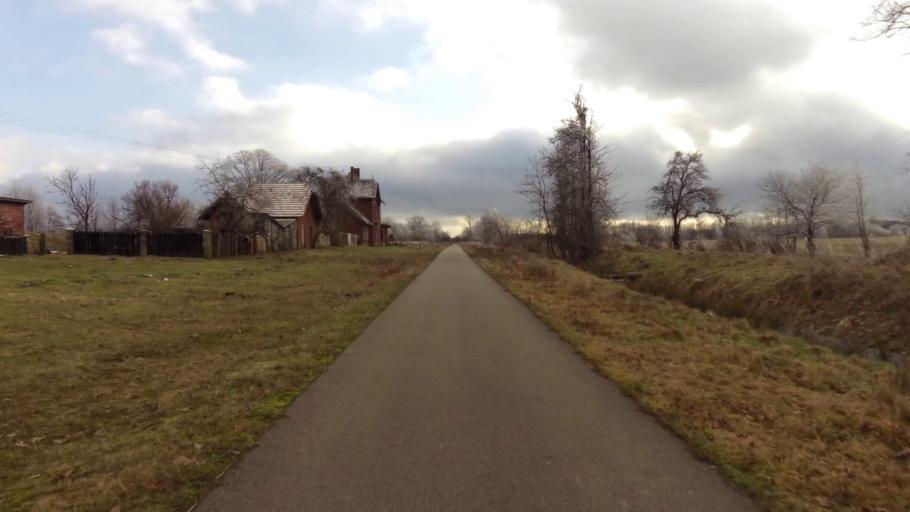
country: PL
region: West Pomeranian Voivodeship
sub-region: Powiat drawski
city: Zlocieniec
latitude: 53.6316
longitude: 16.0559
